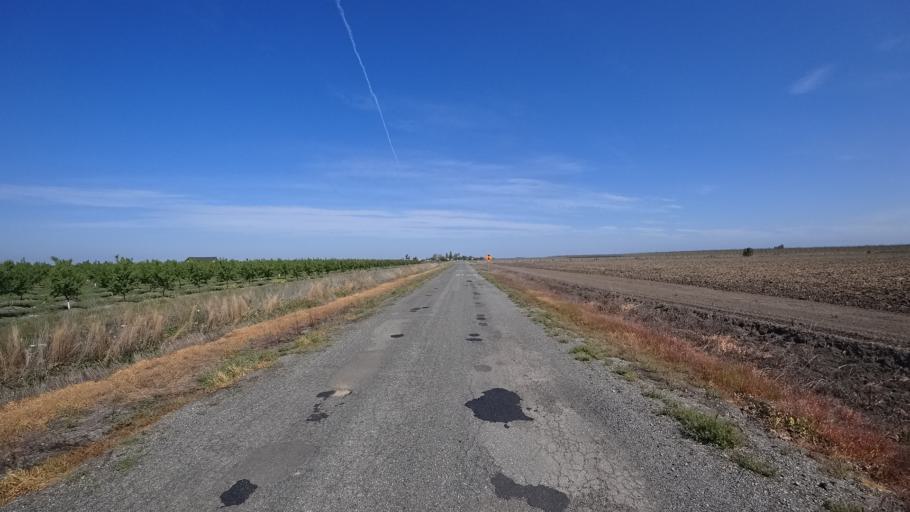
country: US
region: California
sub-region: Glenn County
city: Hamilton City
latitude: 39.6141
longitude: -122.0557
